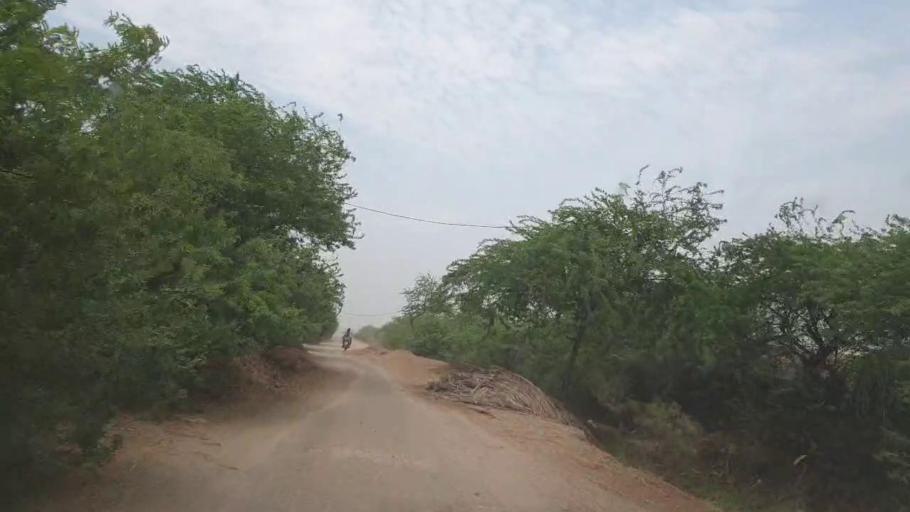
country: PK
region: Sindh
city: Kot Diji
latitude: 27.4403
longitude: 68.7143
